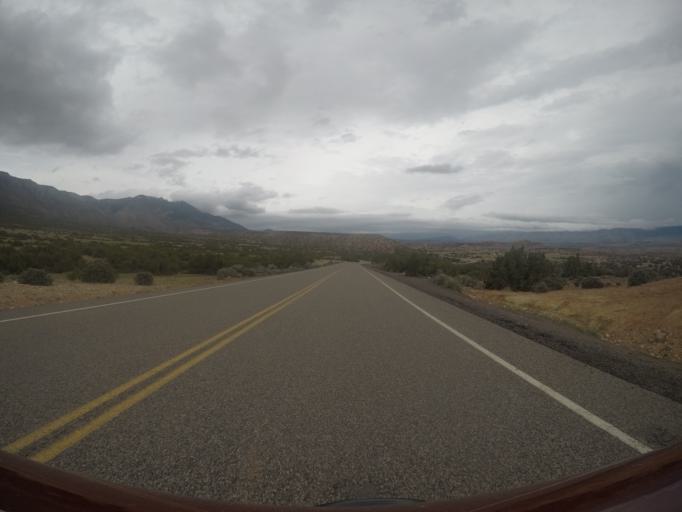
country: US
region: Wyoming
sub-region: Big Horn County
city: Lovell
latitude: 45.0592
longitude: -108.2614
